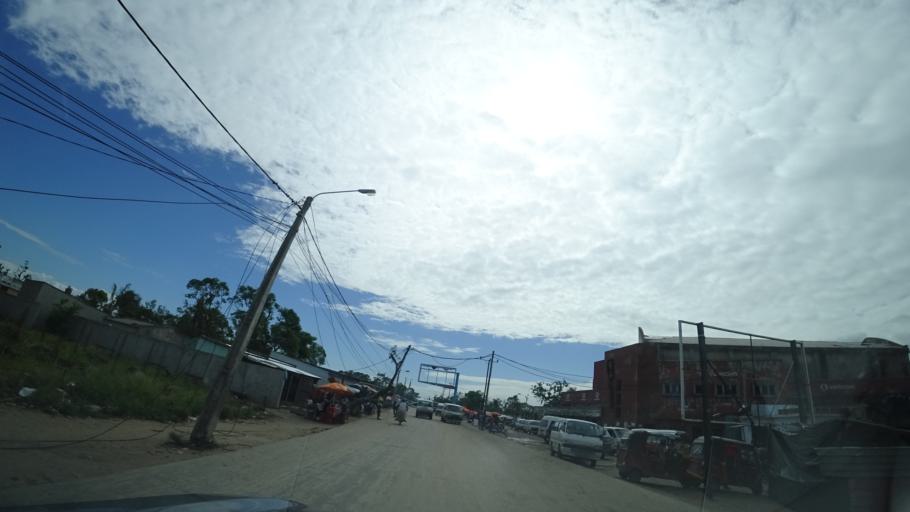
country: MZ
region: Sofala
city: Beira
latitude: -19.7530
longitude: 34.8591
